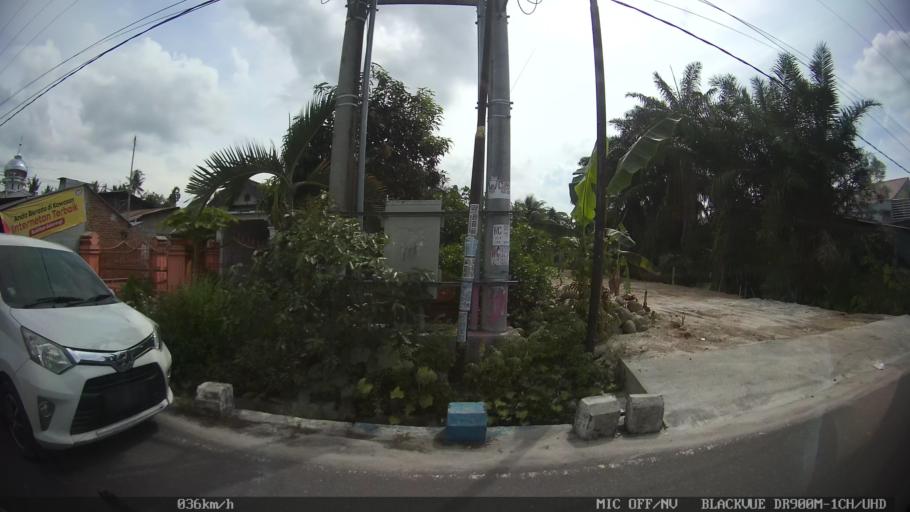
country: ID
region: North Sumatra
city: Percut
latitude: 3.5766
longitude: 98.8666
